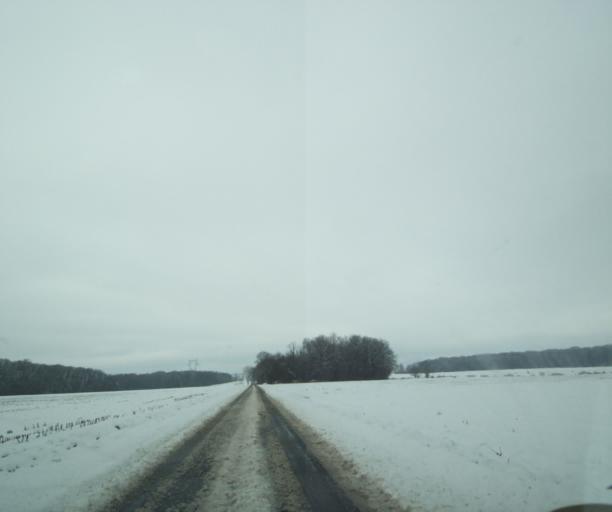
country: FR
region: Champagne-Ardenne
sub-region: Departement de la Haute-Marne
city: Montier-en-Der
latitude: 48.5108
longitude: 4.7549
